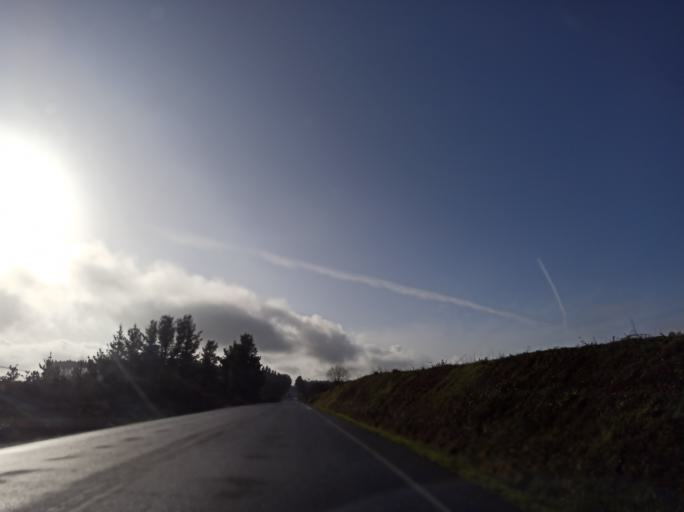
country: ES
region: Galicia
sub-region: Provincia da Coruna
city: Curtis
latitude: 43.1148
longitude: -8.0268
